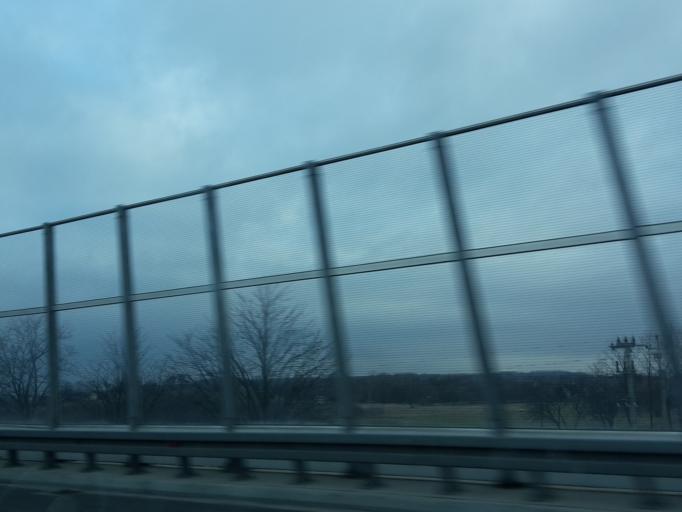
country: PL
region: Warmian-Masurian Voivodeship
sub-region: Powiat elblaski
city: Paslek
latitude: 53.9949
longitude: 19.6914
